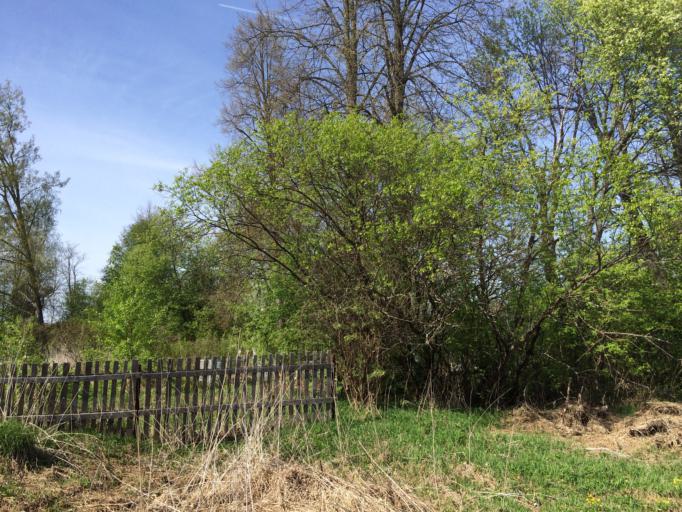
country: RU
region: Jaroslavl
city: Tutayev
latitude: 58.1265
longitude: 39.7970
